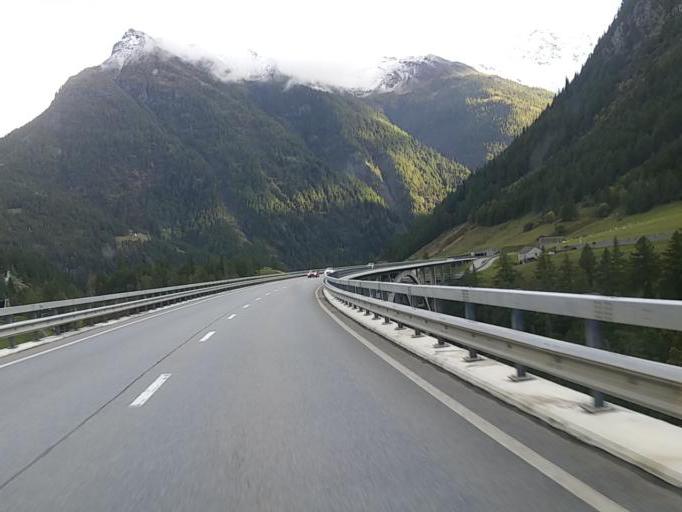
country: IT
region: Piedmont
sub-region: Provincia Verbano-Cusio-Ossola
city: Antronapiana
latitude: 46.1939
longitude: 8.0637
